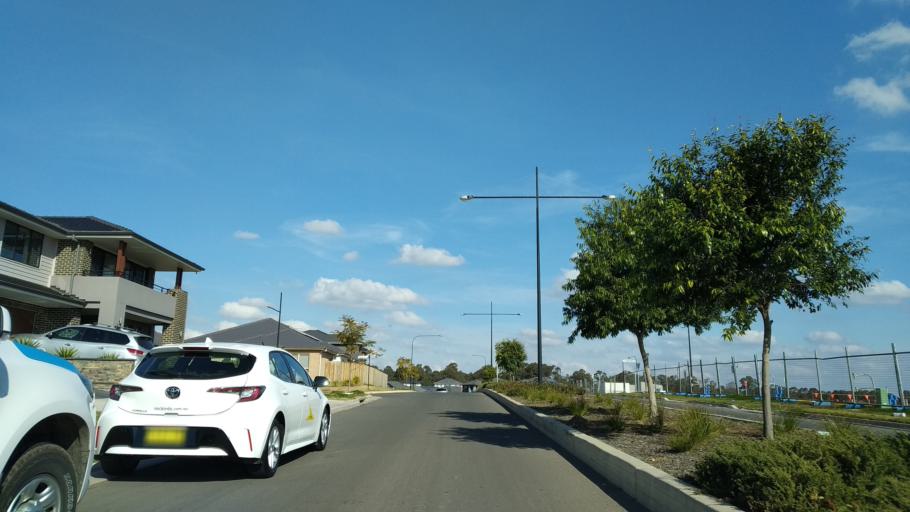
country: AU
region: New South Wales
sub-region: Blacktown
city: Hassall Grove
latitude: -33.7211
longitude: 150.8532
